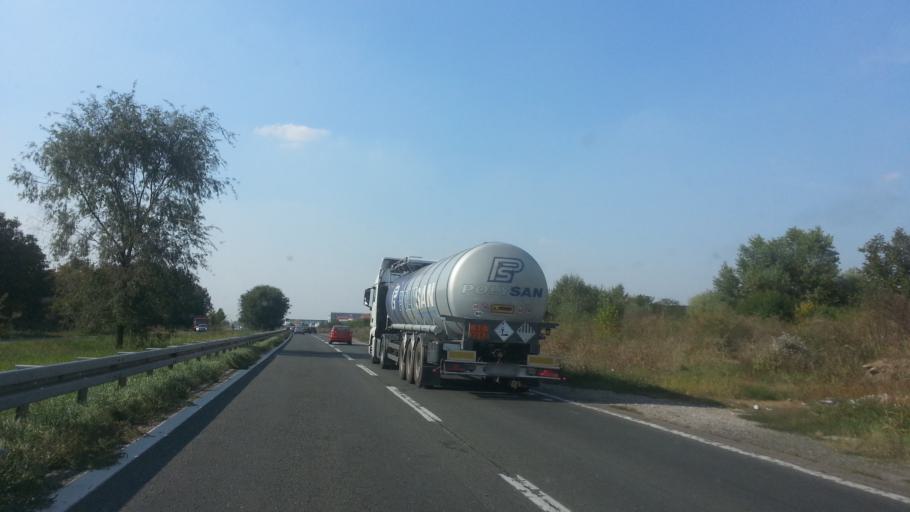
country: RS
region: Central Serbia
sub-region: Belgrade
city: Zemun
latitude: 44.8767
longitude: 20.3270
